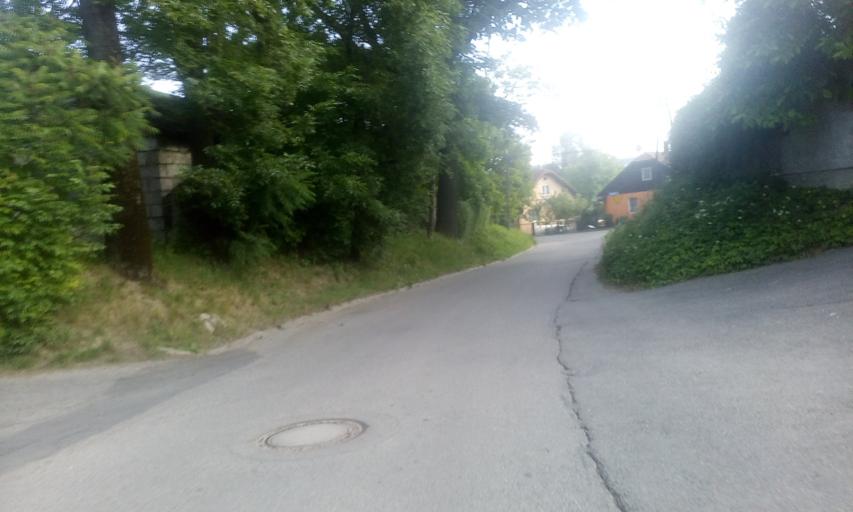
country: PL
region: Lesser Poland Voivodeship
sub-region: Powiat nowosadecki
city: Stary Sacz
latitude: 49.5827
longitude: 20.6643
